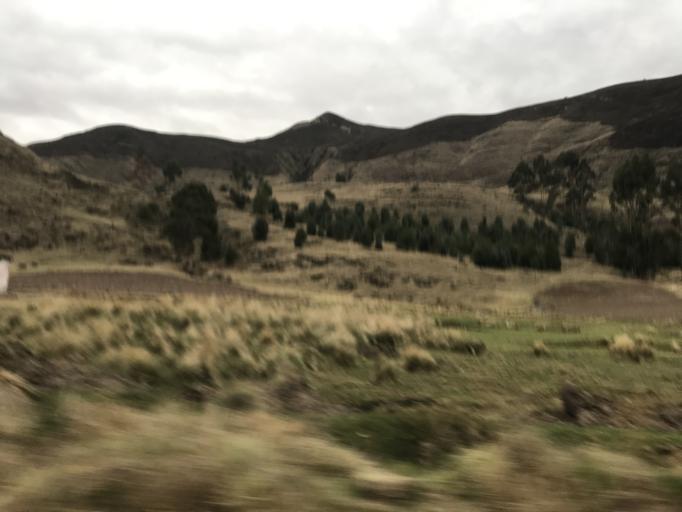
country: PE
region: Cusco
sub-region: Provincia de Anta
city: Huarocondo
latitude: -13.4420
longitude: -72.2061
